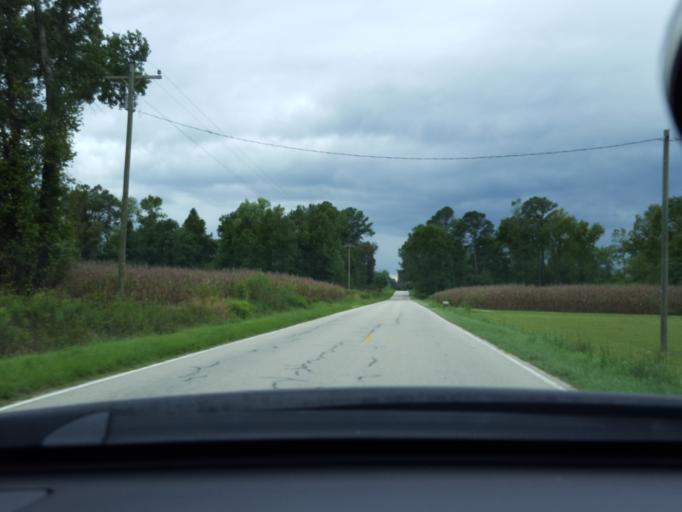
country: US
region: North Carolina
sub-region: Duplin County
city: Rose Hill
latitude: 34.8075
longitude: -78.2008
